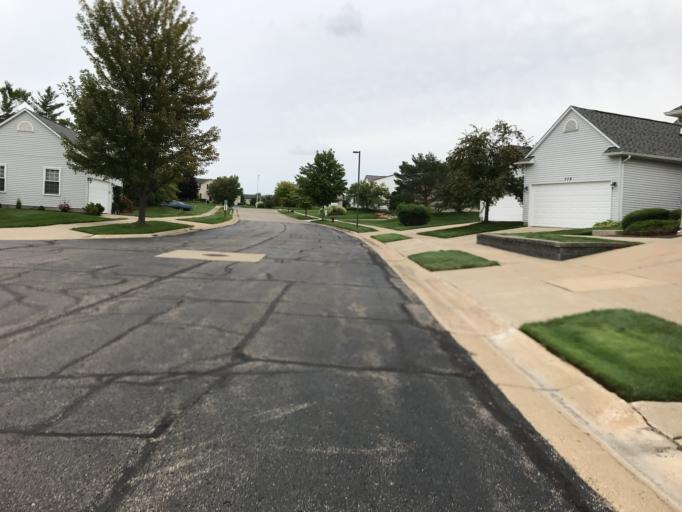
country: US
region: Michigan
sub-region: Oakland County
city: South Lyon
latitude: 42.4739
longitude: -83.6413
